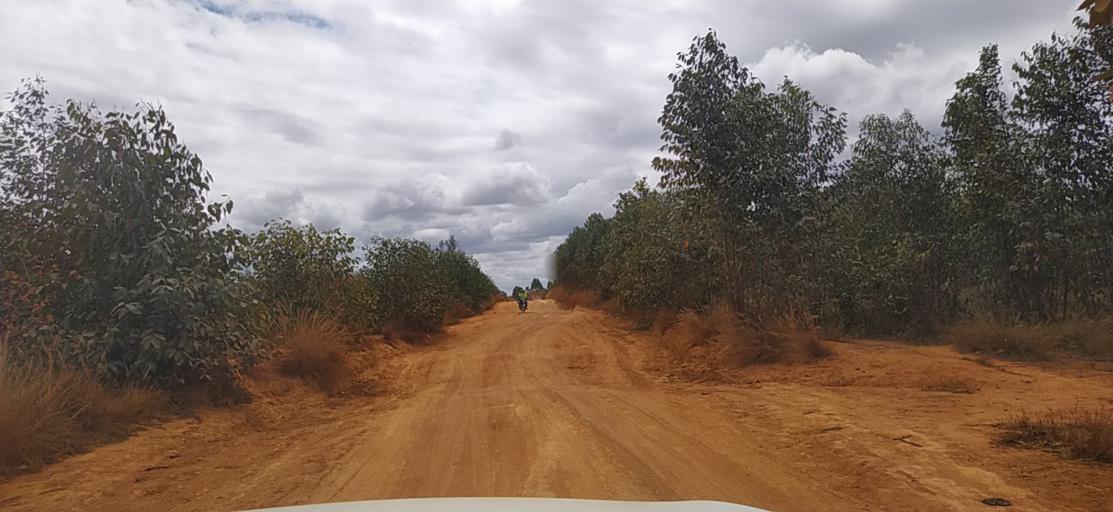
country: MG
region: Alaotra Mangoro
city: Ambatondrazaka
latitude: -18.0637
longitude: 48.2571
